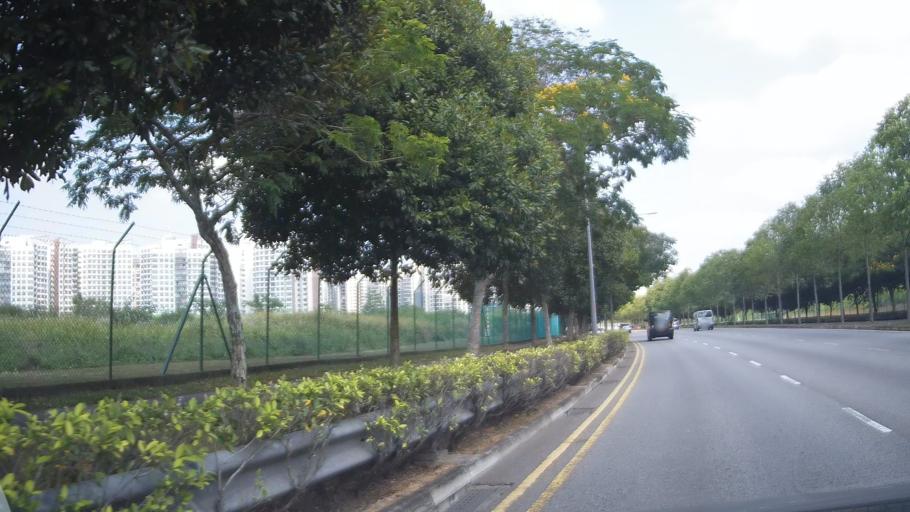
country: MY
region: Johor
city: Kampung Pasir Gudang Baru
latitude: 1.3785
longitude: 103.9080
